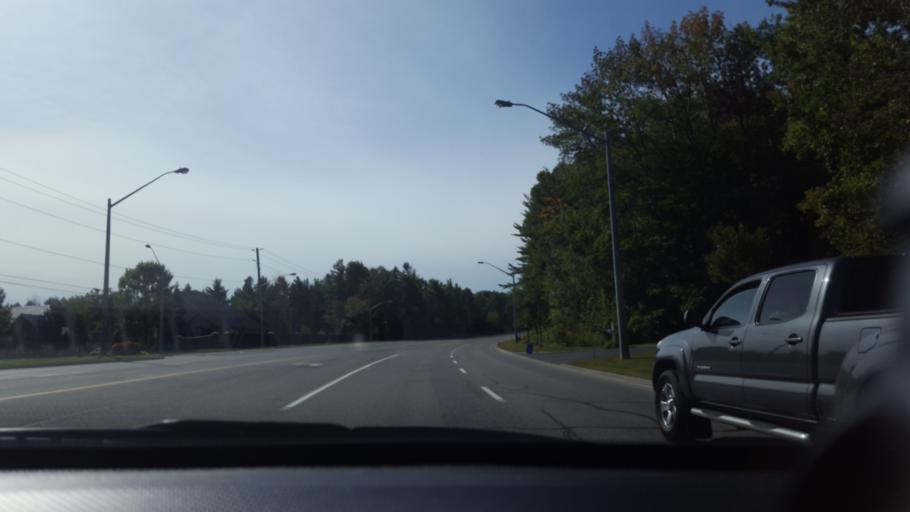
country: CA
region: Ontario
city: Newmarket
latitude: 44.0282
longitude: -79.4957
